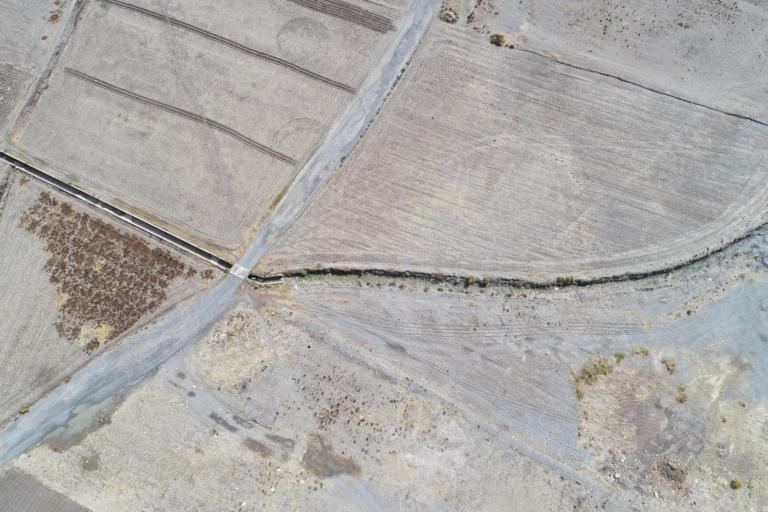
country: BO
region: La Paz
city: Achacachi
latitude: -16.0375
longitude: -68.6828
